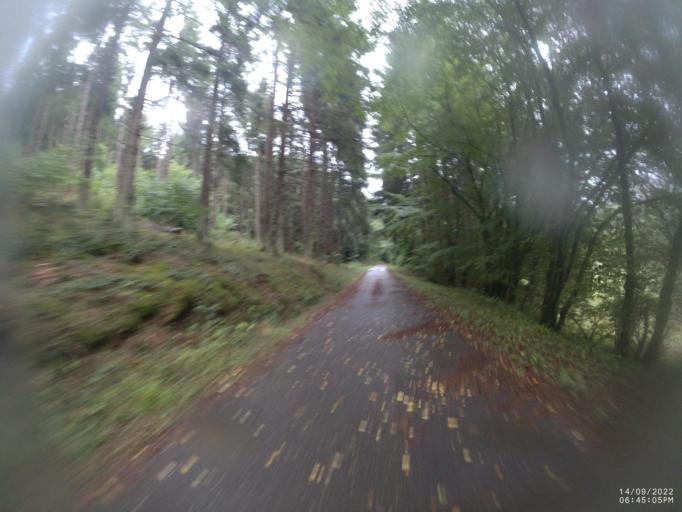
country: DE
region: Rheinland-Pfalz
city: Nohn
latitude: 50.3587
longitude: 6.7769
